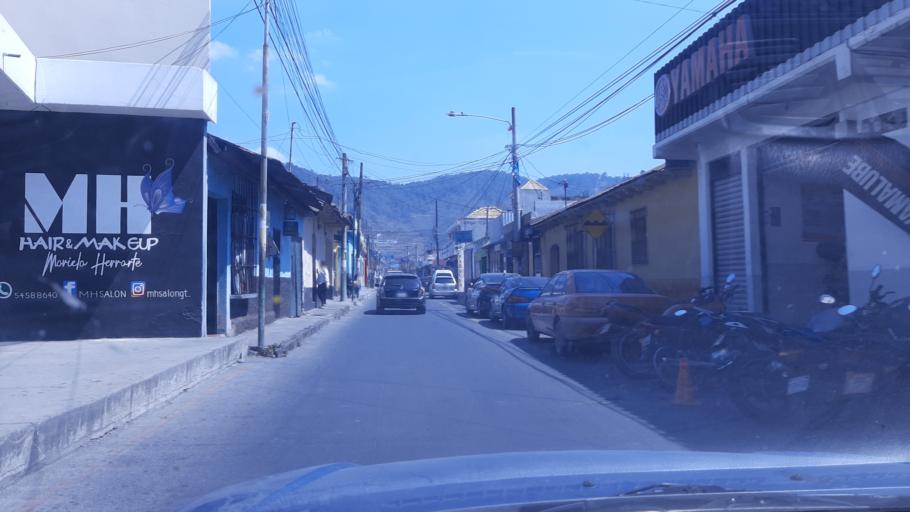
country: GT
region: Guatemala
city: Amatitlan
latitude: 14.4811
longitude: -90.6209
